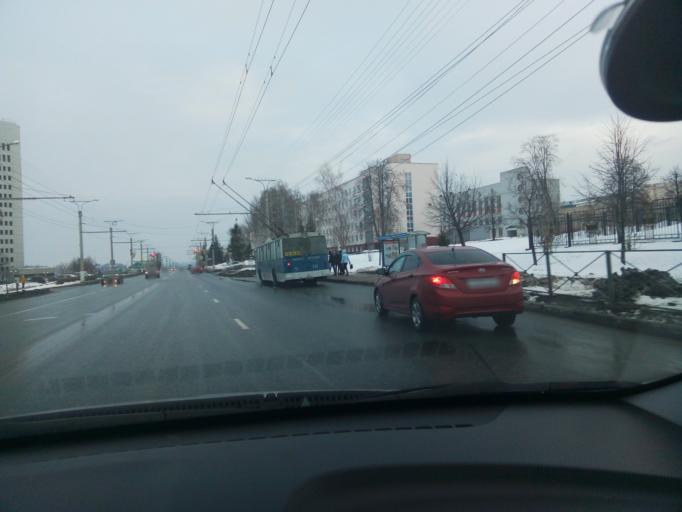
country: RU
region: Chuvashia
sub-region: Cheboksarskiy Rayon
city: Cheboksary
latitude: 56.1377
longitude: 47.2431
